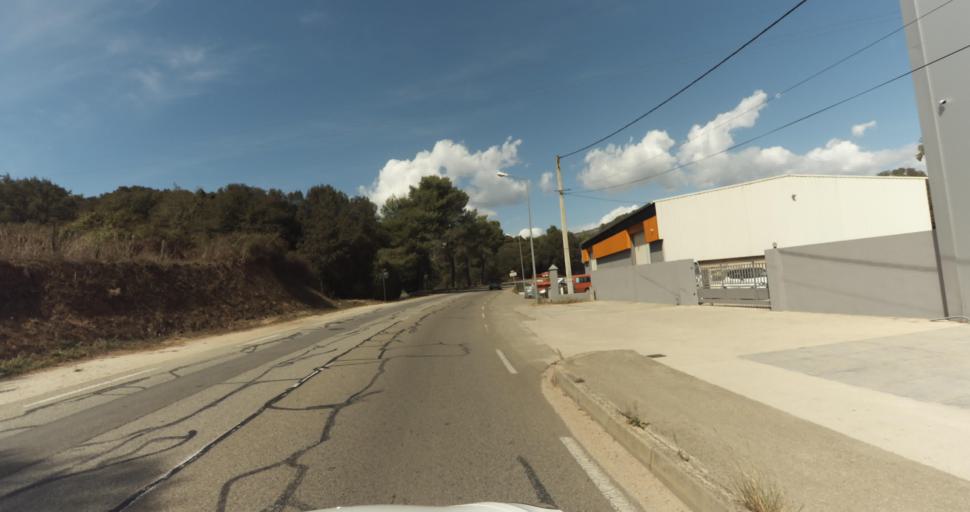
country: FR
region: Corsica
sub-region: Departement de la Corse-du-Sud
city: Afa
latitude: 41.9588
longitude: 8.7805
